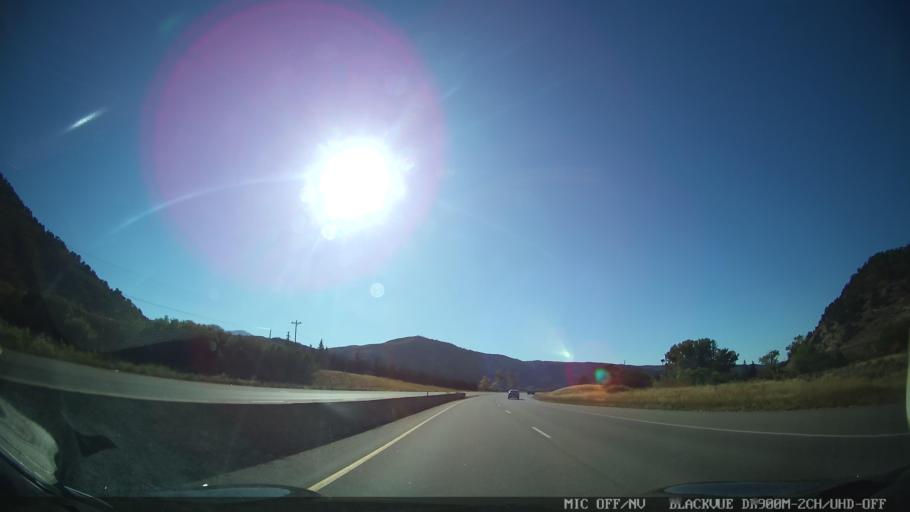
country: US
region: Colorado
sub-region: Eagle County
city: Basalt
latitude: 39.3647
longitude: -107.0552
